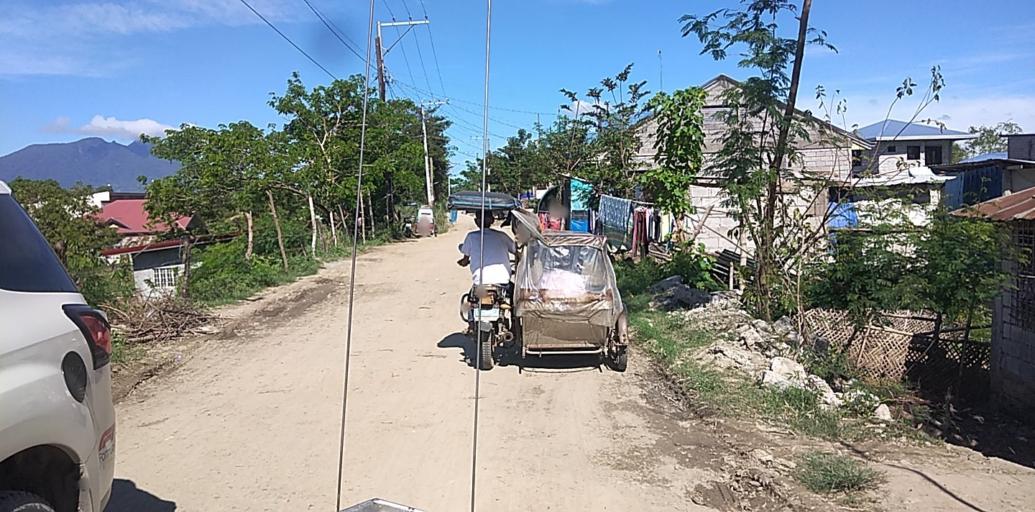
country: PH
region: Central Luzon
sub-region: Province of Pampanga
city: Candaba
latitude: 15.1207
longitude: 120.8133
